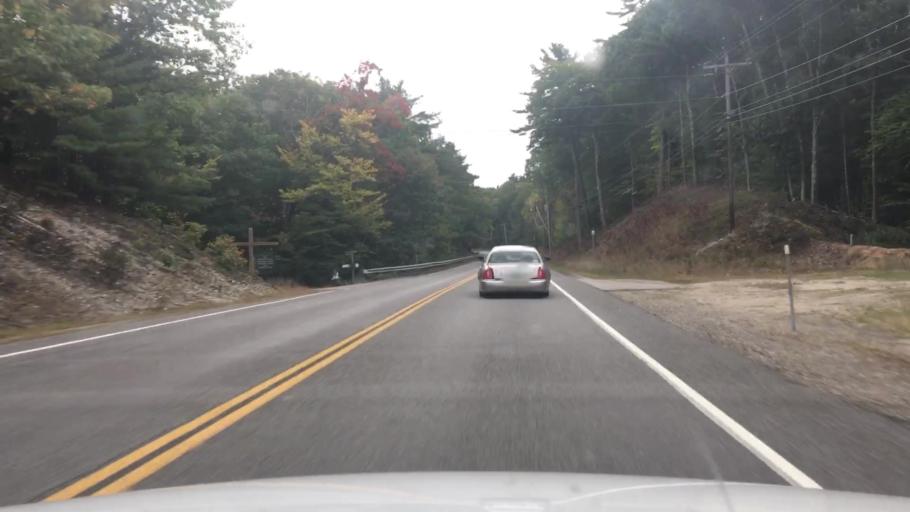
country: US
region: New Hampshire
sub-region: Strafford County
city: New Durham
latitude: 43.4923
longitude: -71.2550
